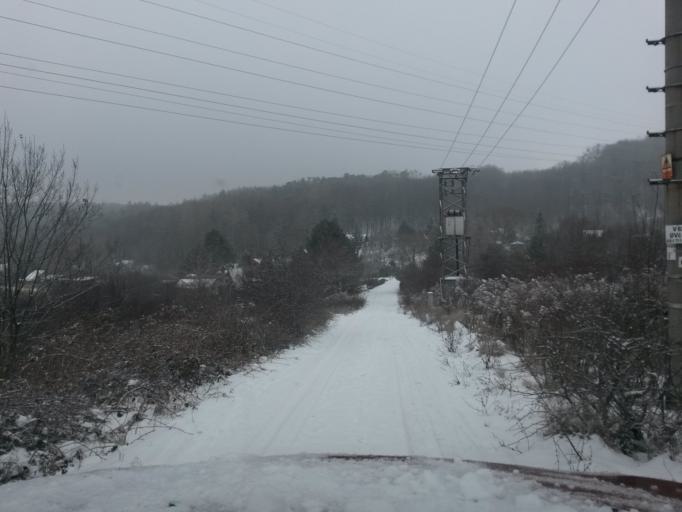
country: SK
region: Kosicky
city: Kosice
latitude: 48.7247
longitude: 21.3035
